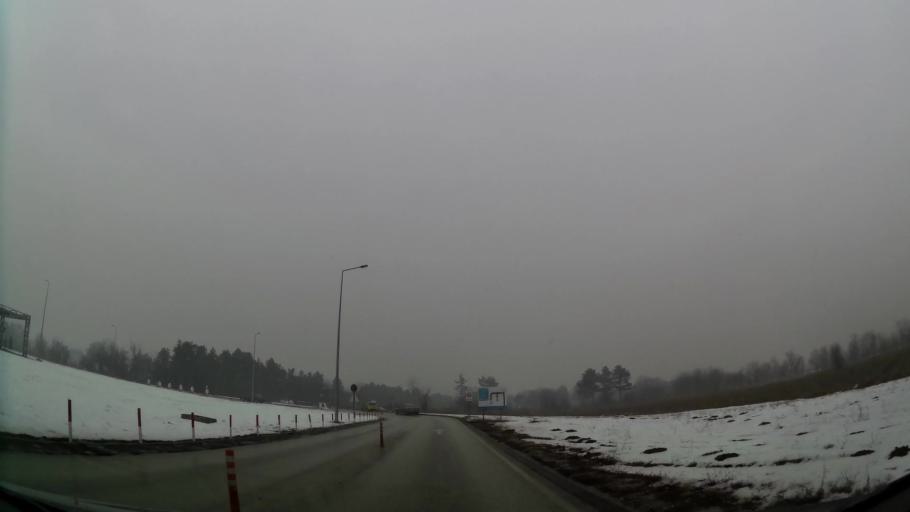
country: MK
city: Miladinovci
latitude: 41.9627
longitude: 21.6294
